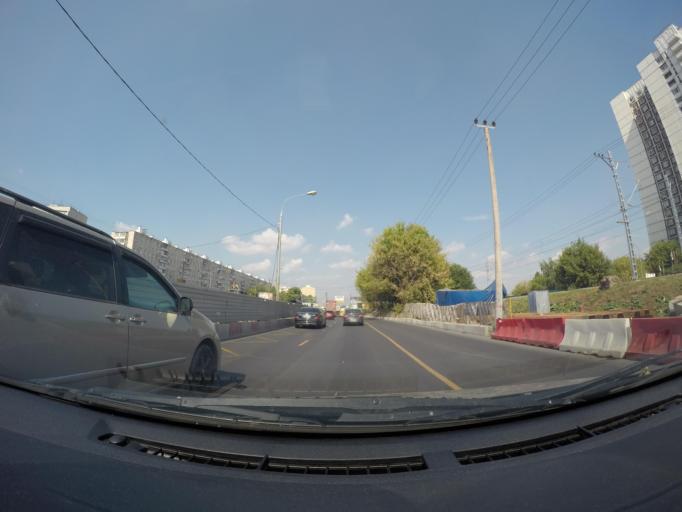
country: RU
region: Moscow
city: Likhobory
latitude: 55.8294
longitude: 37.5731
